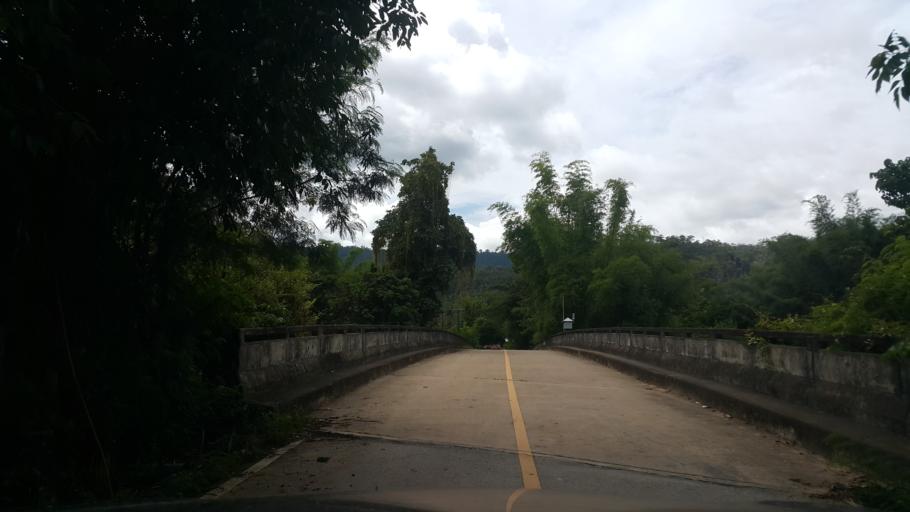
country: TH
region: Phitsanulok
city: Chat Trakan
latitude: 17.3030
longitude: 100.6709
